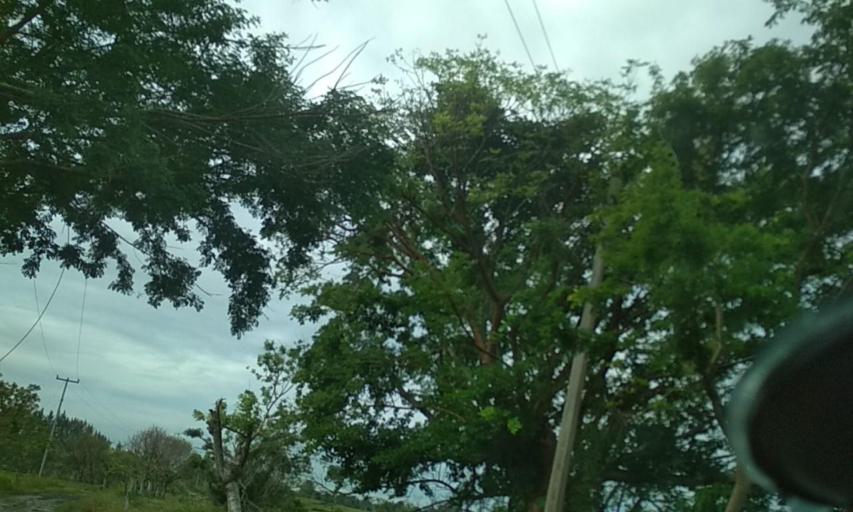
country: MX
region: Veracruz
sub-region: Cazones de Herrera
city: Rancho Nuevo
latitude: 20.6028
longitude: -97.1460
